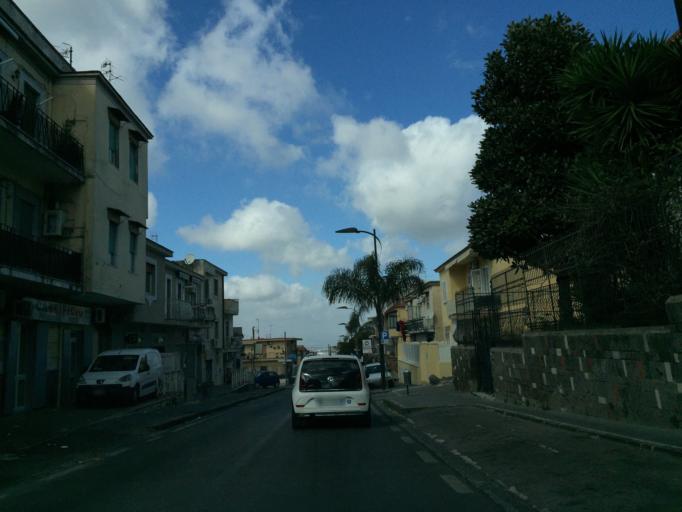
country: IT
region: Campania
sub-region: Provincia di Napoli
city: Massa di Somma
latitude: 40.8487
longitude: 14.3752
